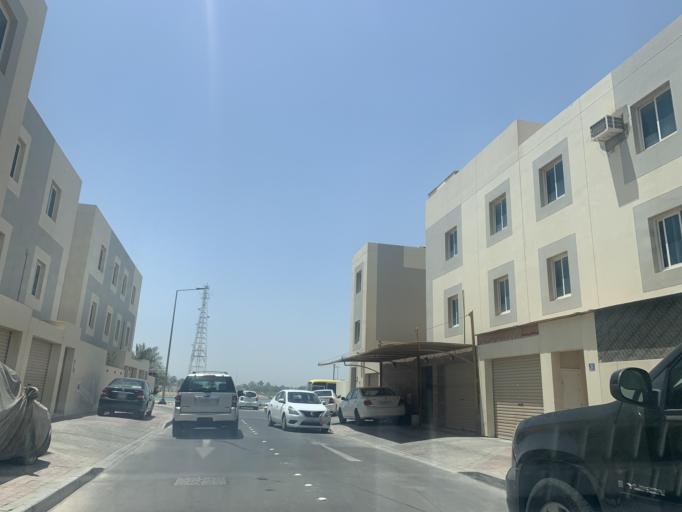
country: BH
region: Manama
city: Jidd Hafs
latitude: 26.2361
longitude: 50.4693
